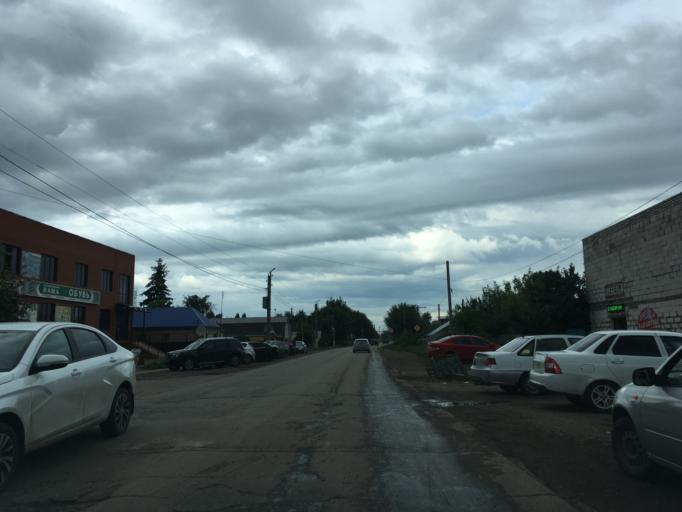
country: RU
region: Samara
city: Bezenchuk
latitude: 52.9810
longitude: 49.4320
